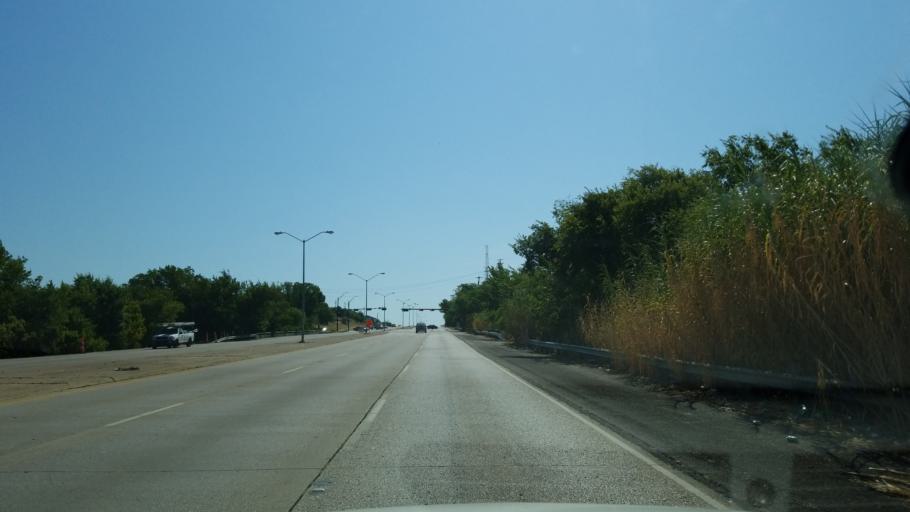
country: US
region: Texas
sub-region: Dallas County
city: Cockrell Hill
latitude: 32.7496
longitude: -96.9048
